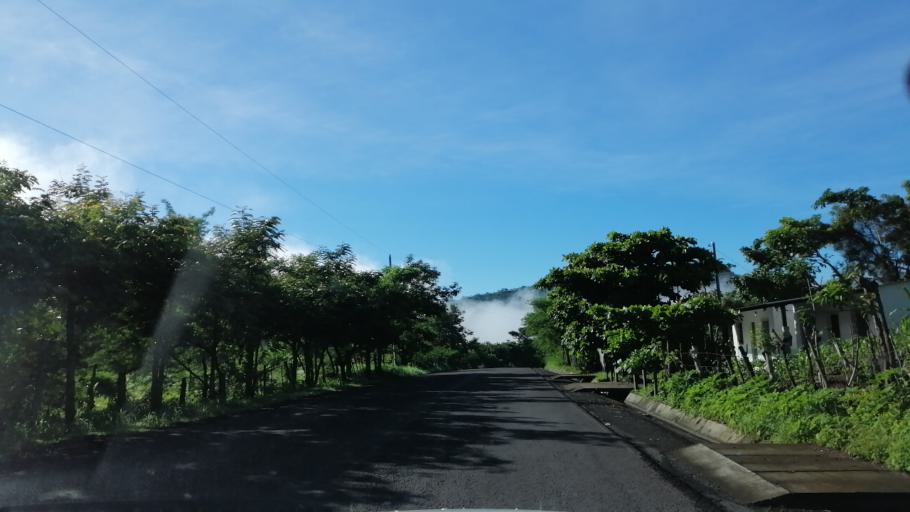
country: SV
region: Morazan
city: Cacaopera
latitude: 13.7778
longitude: -88.0978
